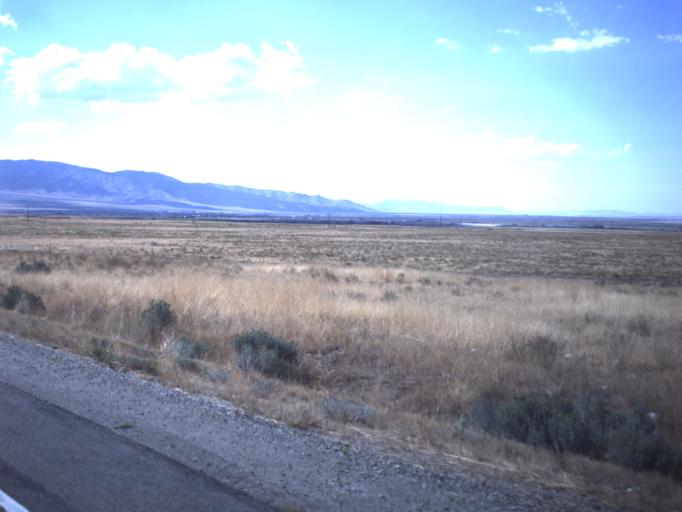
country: US
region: Utah
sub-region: Tooele County
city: Tooele
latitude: 40.5509
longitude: -112.3193
